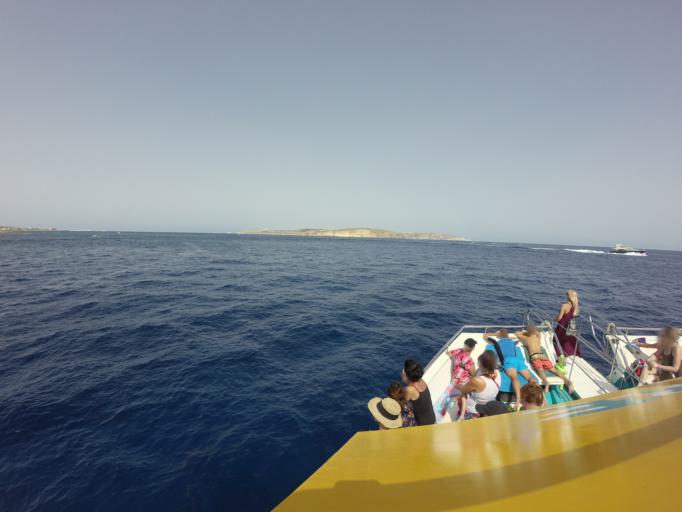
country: MT
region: Il-Mellieha
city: Mellieha
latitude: 35.9992
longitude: 14.3681
